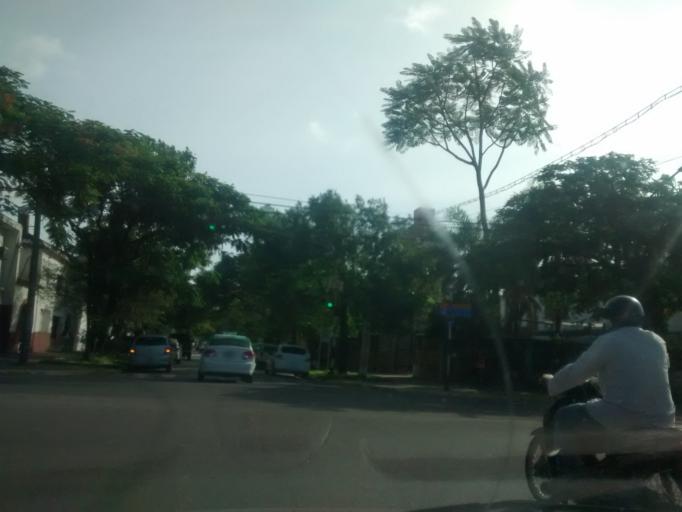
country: AR
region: Chaco
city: Resistencia
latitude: -27.4560
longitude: -58.9814
